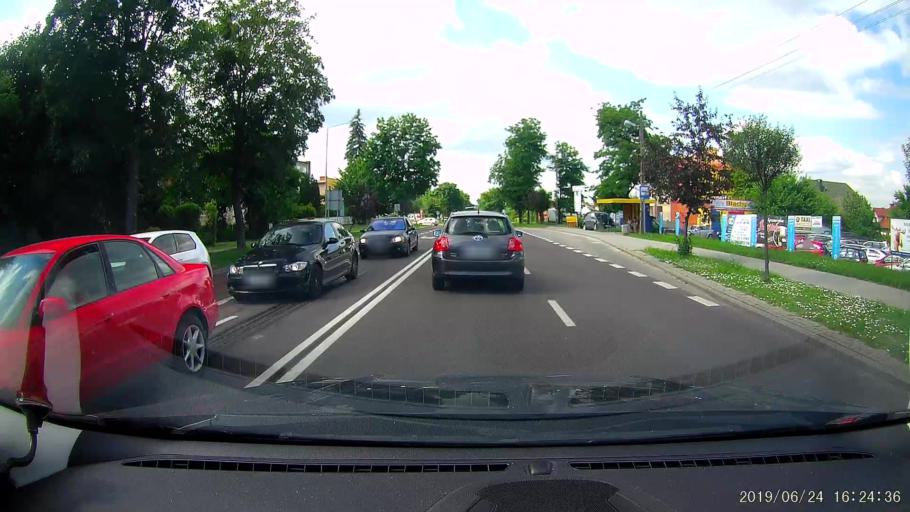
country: PL
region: Lublin Voivodeship
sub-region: Powiat tomaszowski
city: Tomaszow Lubelski
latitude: 50.4367
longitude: 23.4198
